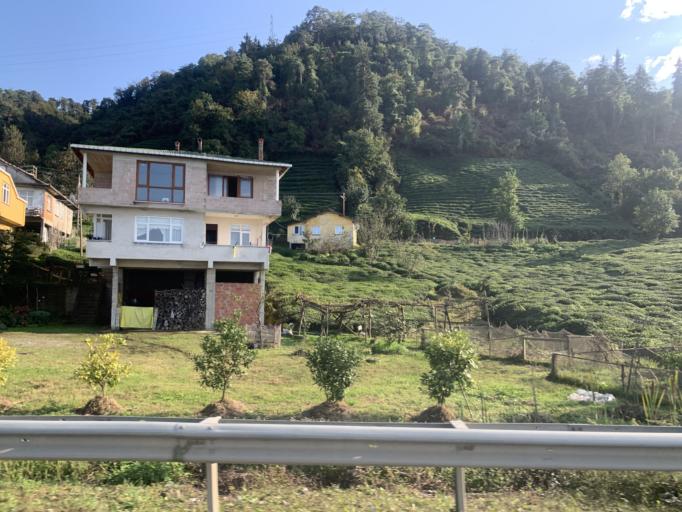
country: TR
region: Trabzon
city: Of
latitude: 40.9365
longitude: 40.2498
